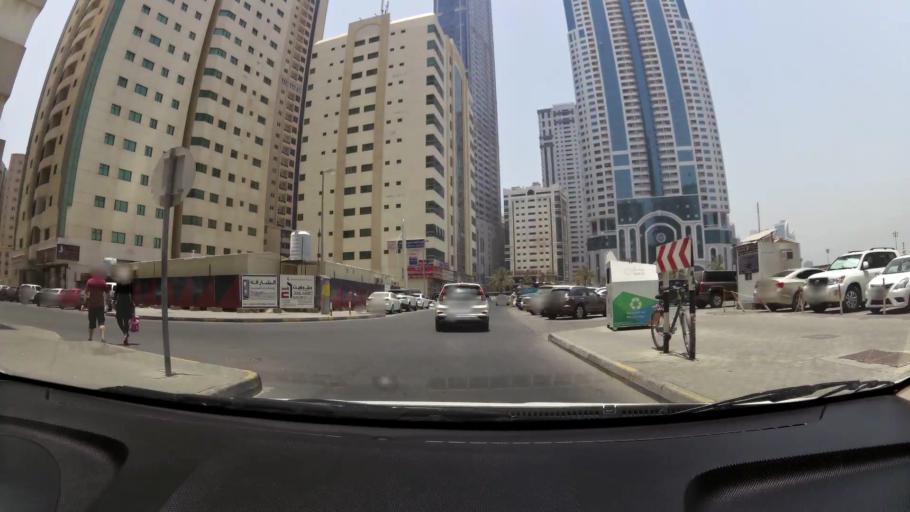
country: AE
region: Ash Shariqah
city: Sharjah
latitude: 25.3235
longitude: 55.3816
